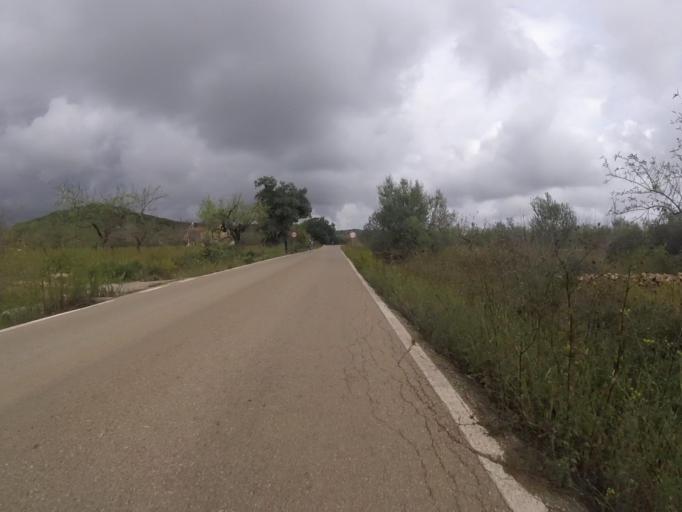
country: ES
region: Valencia
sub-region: Provincia de Castello
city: Cabanes
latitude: 40.1534
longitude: 0.0908
